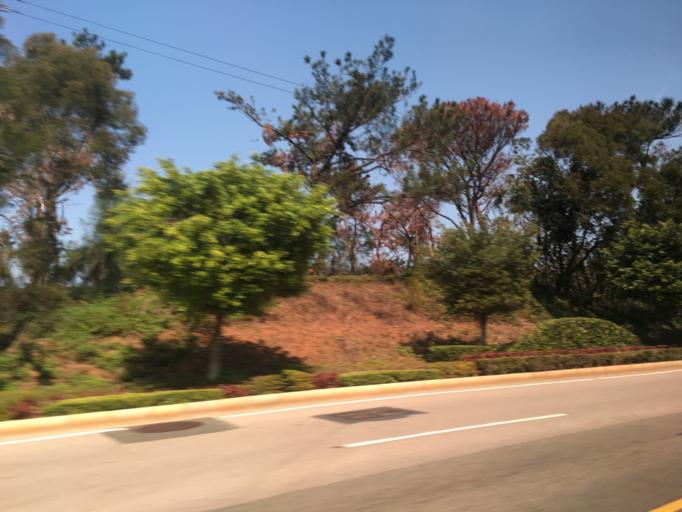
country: TW
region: Fukien
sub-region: Kinmen
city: Jincheng
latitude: 24.4357
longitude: 118.3507
